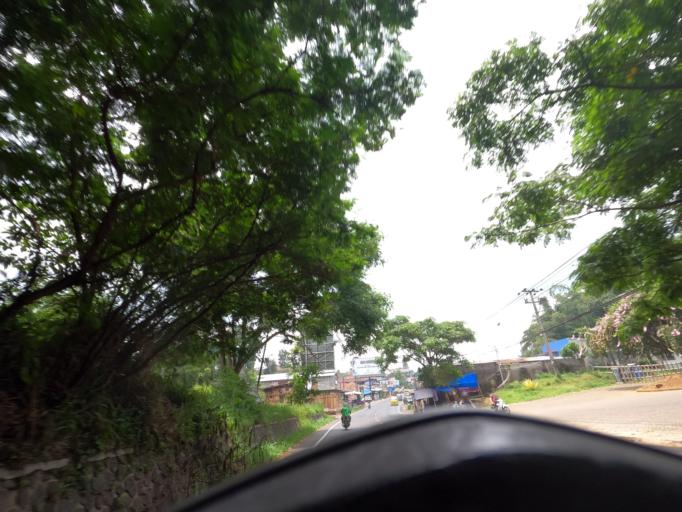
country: ID
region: West Java
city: Sukabumi
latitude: -6.7559
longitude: 107.0465
